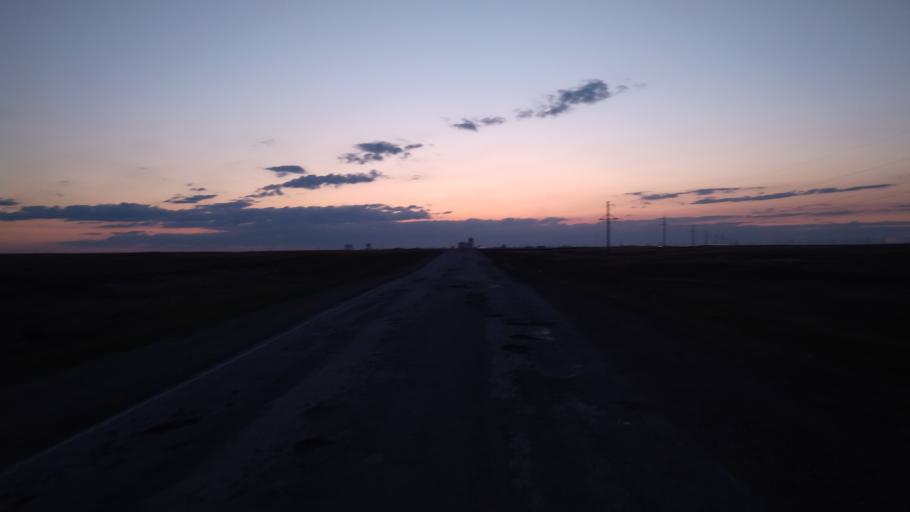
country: RU
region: Chelyabinsk
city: Troitsk
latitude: 54.0923
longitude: 61.6403
